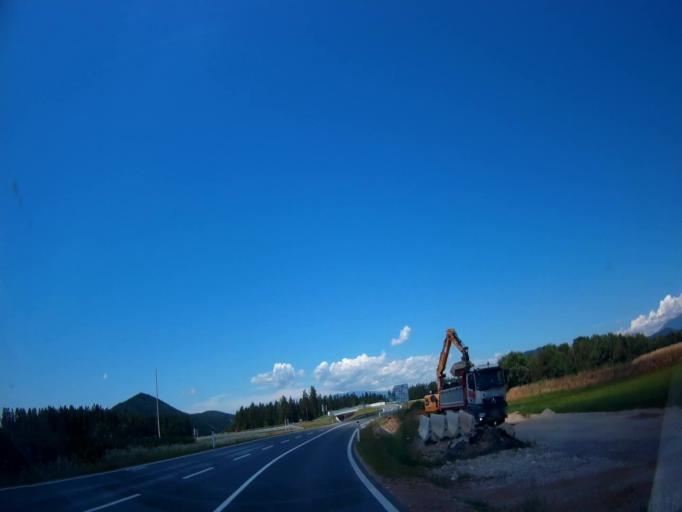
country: AT
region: Carinthia
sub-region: Politischer Bezirk Volkermarkt
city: Bleiburg/Pliberk
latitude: 46.6075
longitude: 14.7835
